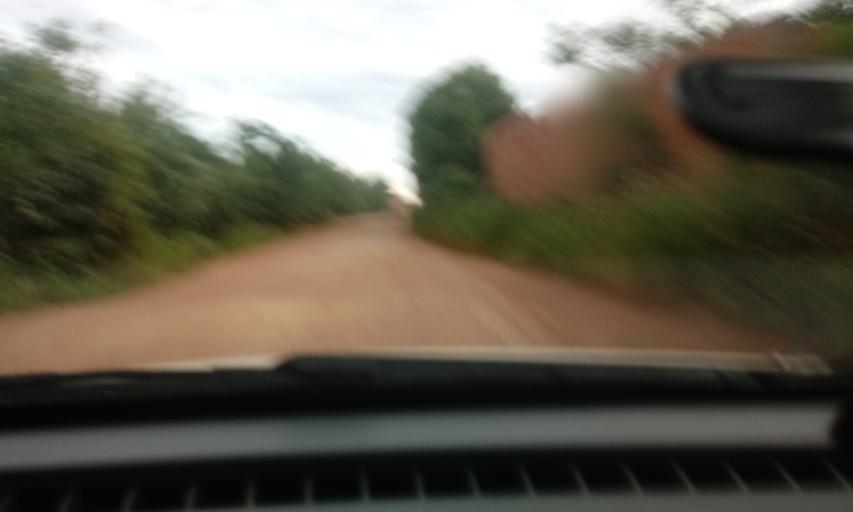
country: BR
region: Bahia
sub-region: Riacho De Santana
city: Riacho de Santana
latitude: -13.7825
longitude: -42.7235
